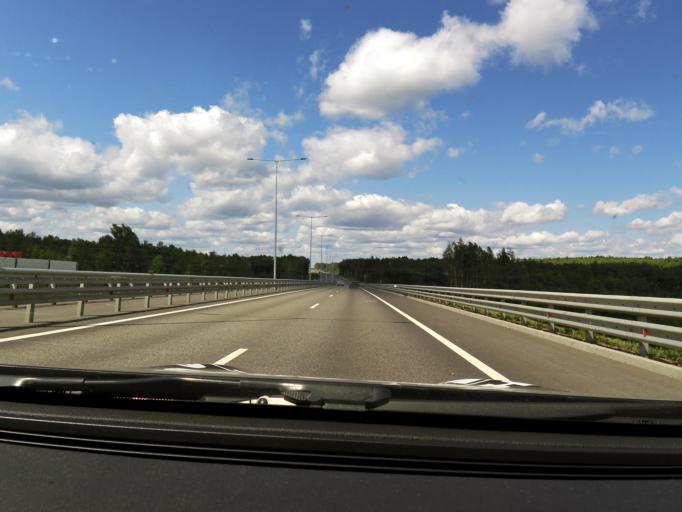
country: RU
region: Tverskaya
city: Vydropuzhsk
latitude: 57.3690
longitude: 34.6498
